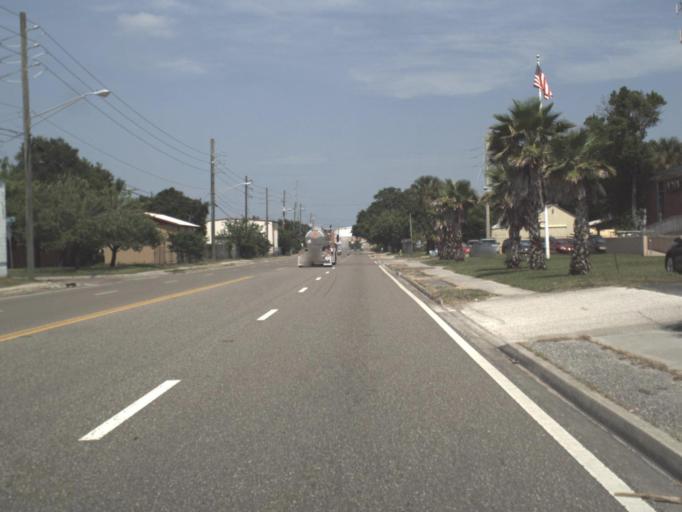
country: US
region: Florida
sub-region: Duval County
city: Jacksonville
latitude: 30.3575
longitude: -81.6312
